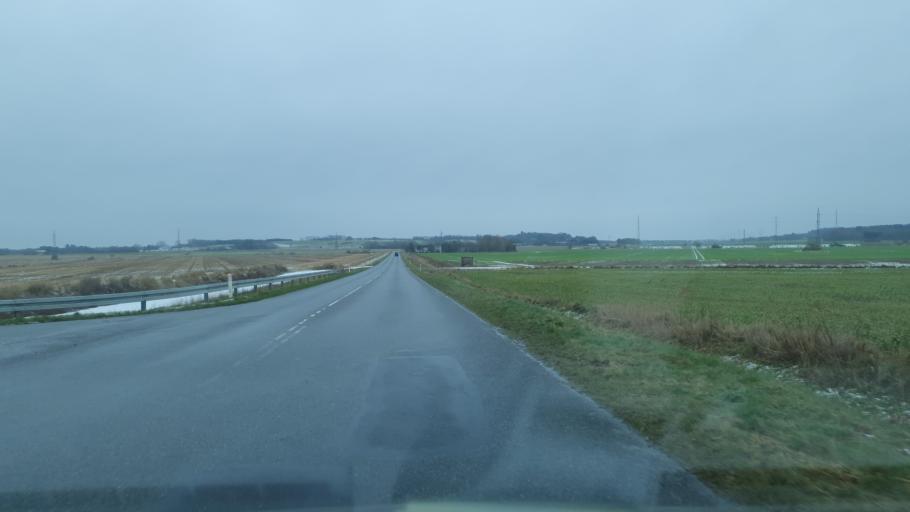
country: DK
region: North Denmark
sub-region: Jammerbugt Kommune
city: Brovst
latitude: 57.1227
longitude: 9.4916
